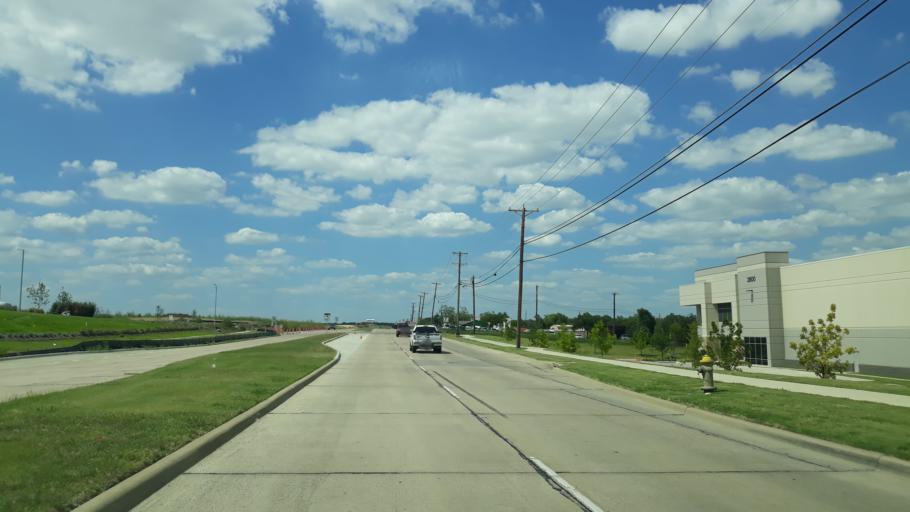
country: US
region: Texas
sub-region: Tarrant County
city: Euless
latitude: 32.8440
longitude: -97.0217
